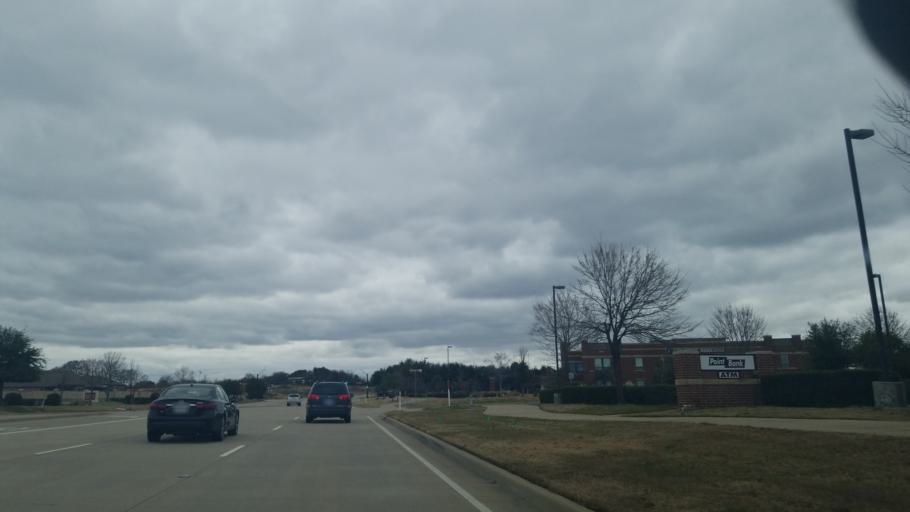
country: US
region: Texas
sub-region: Denton County
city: Double Oak
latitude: 33.0527
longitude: -97.0741
